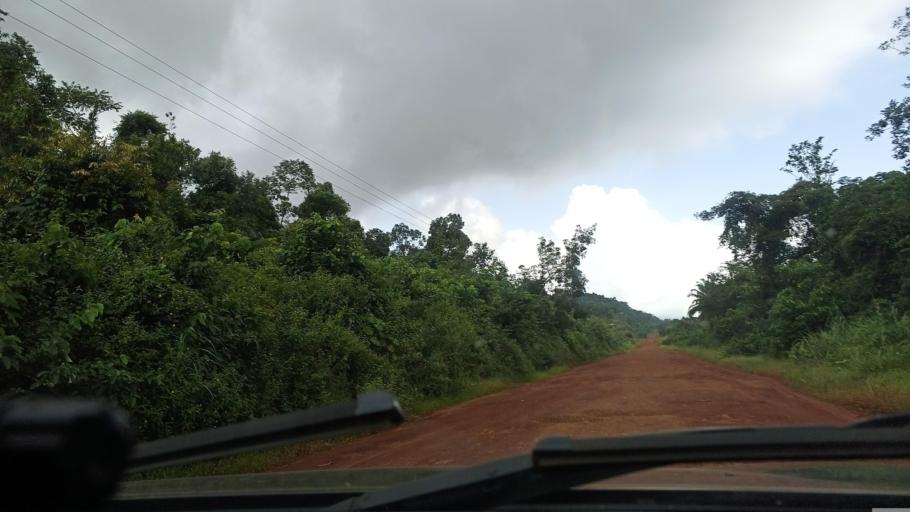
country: LR
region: Grand Cape Mount
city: Robertsport
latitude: 6.7107
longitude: -11.3353
